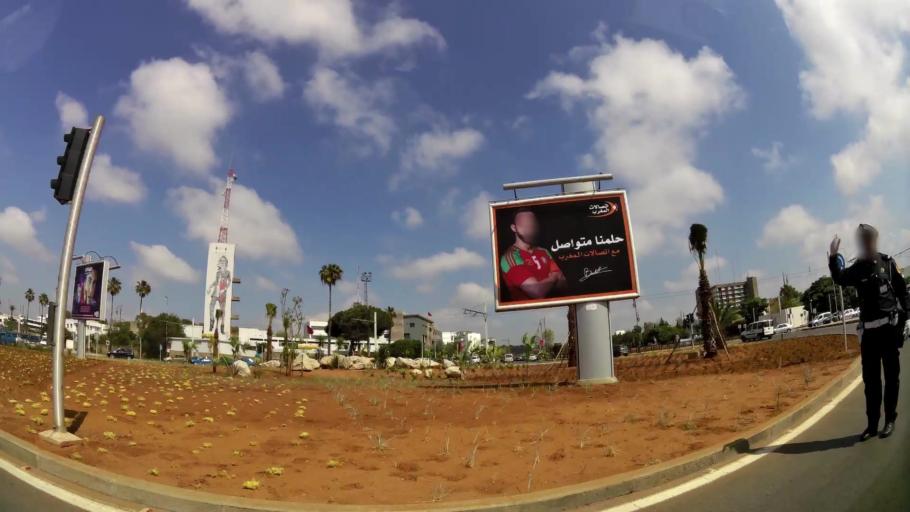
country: MA
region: Rabat-Sale-Zemmour-Zaer
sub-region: Rabat
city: Rabat
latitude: 33.9903
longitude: -6.8576
